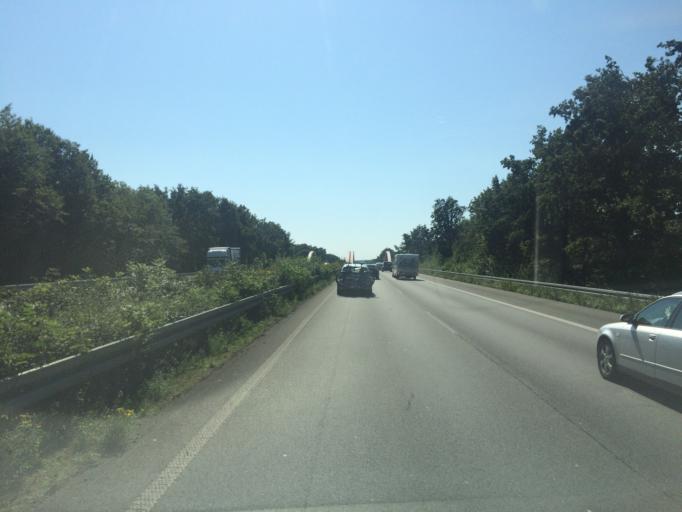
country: DE
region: North Rhine-Westphalia
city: Werne
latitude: 51.6621
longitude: 7.6827
